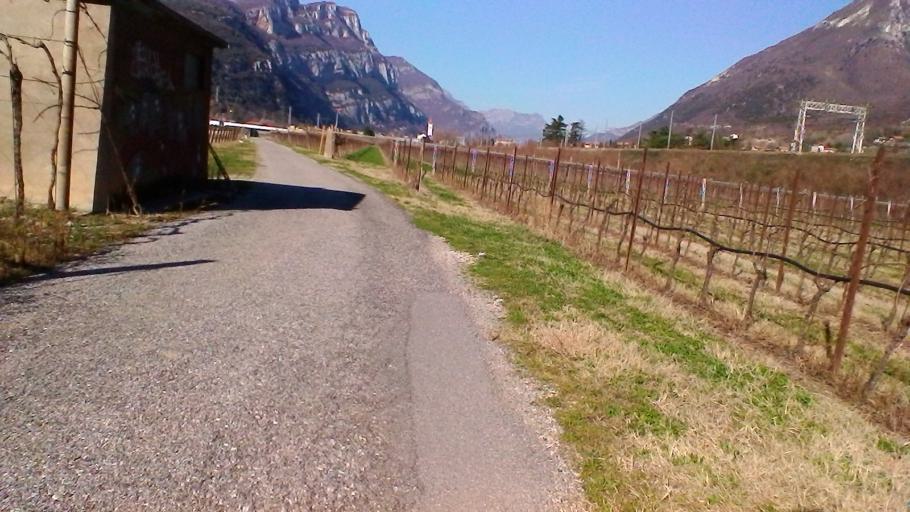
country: IT
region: Veneto
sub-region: Provincia di Verona
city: Dolce
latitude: 45.5952
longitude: 10.8474
